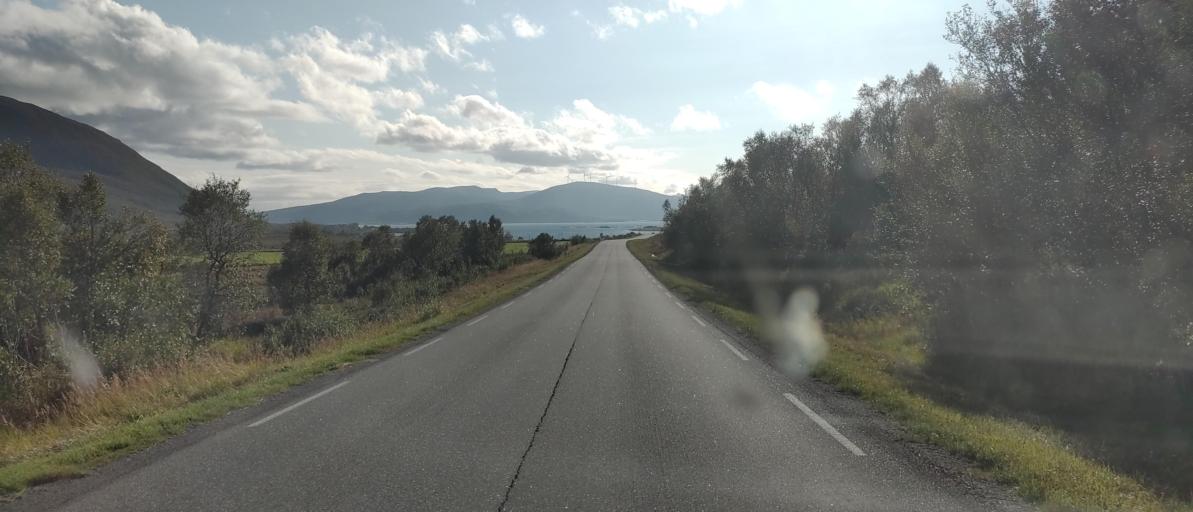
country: NO
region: Nordland
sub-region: Sortland
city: Sortland
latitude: 68.7907
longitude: 15.5023
